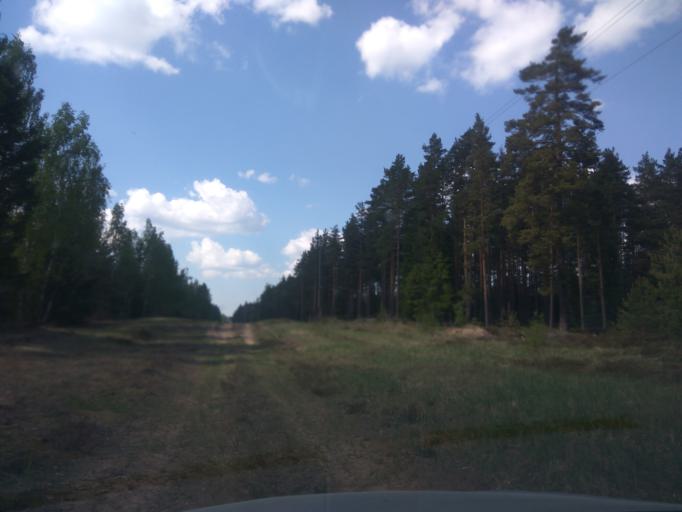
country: LV
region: Kuldigas Rajons
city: Kuldiga
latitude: 57.1822
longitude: 21.9995
